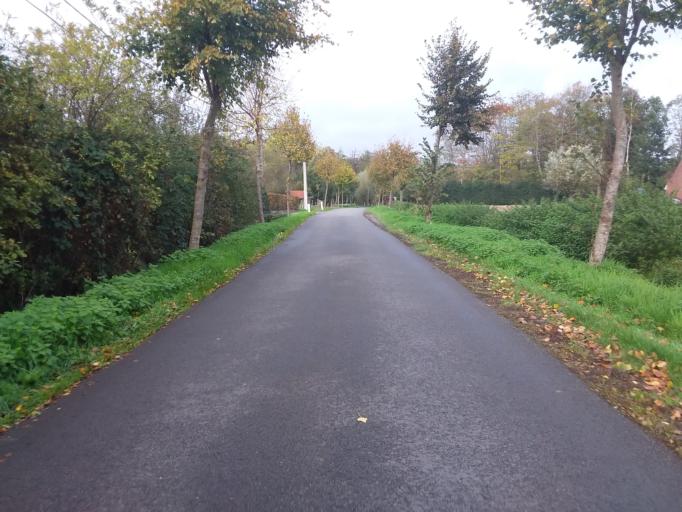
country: BE
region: Flanders
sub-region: Provincie Oost-Vlaanderen
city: Zulte
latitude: 50.9373
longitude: 3.4782
